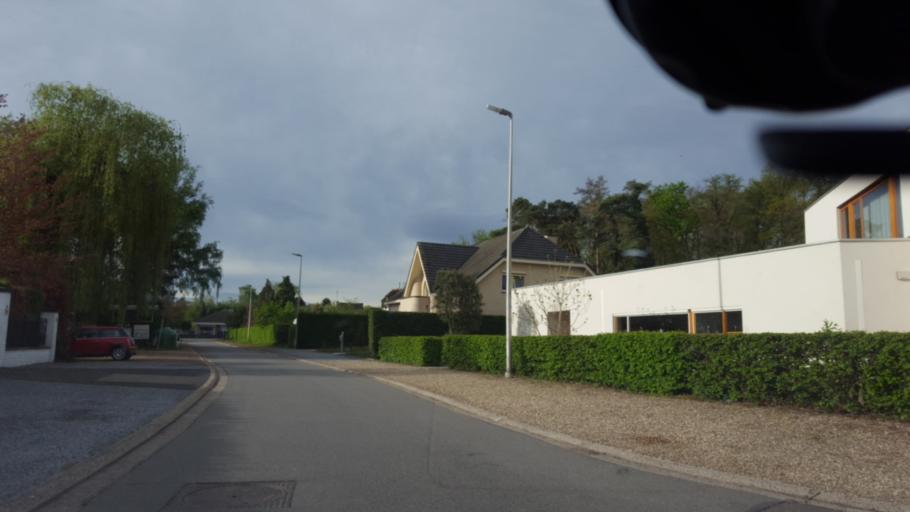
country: BE
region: Flanders
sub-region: Provincie Limburg
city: Lanaken
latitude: 50.9110
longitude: 5.6749
